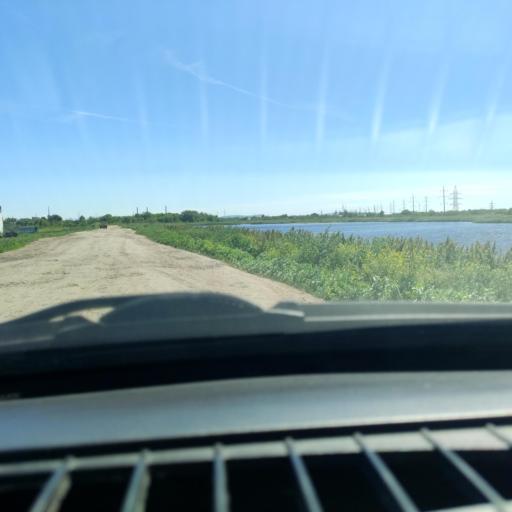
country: RU
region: Samara
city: Tol'yatti
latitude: 53.5934
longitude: 49.4384
